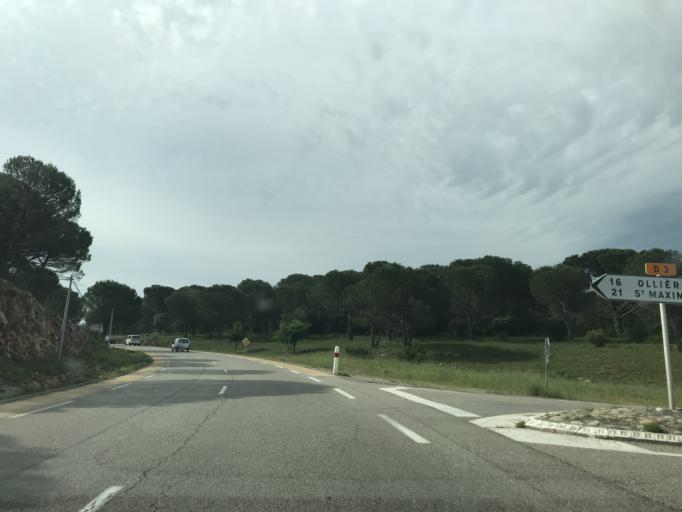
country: FR
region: Provence-Alpes-Cote d'Azur
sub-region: Departement du Var
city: Rians
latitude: 43.5870
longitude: 5.7490
